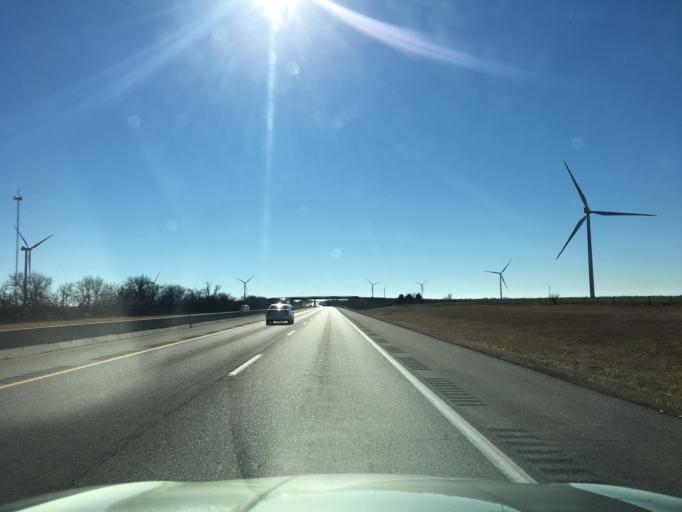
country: US
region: Kansas
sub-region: Sumner County
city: Wellington
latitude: 37.1485
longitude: -97.3395
